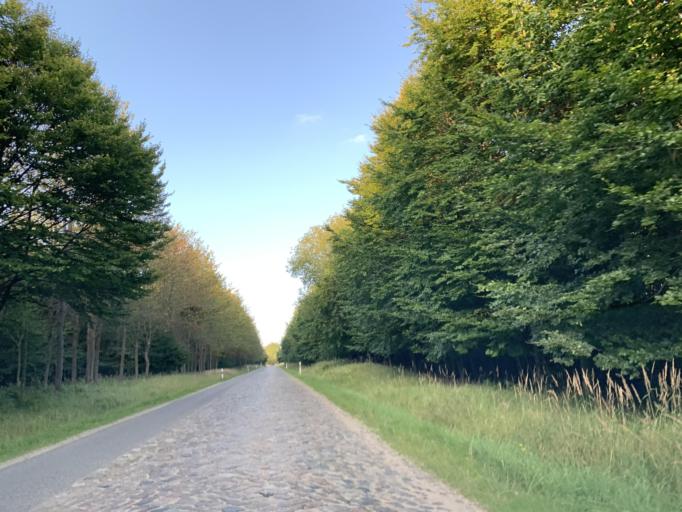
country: DE
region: Mecklenburg-Vorpommern
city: Loitz
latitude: 53.3566
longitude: 13.4323
